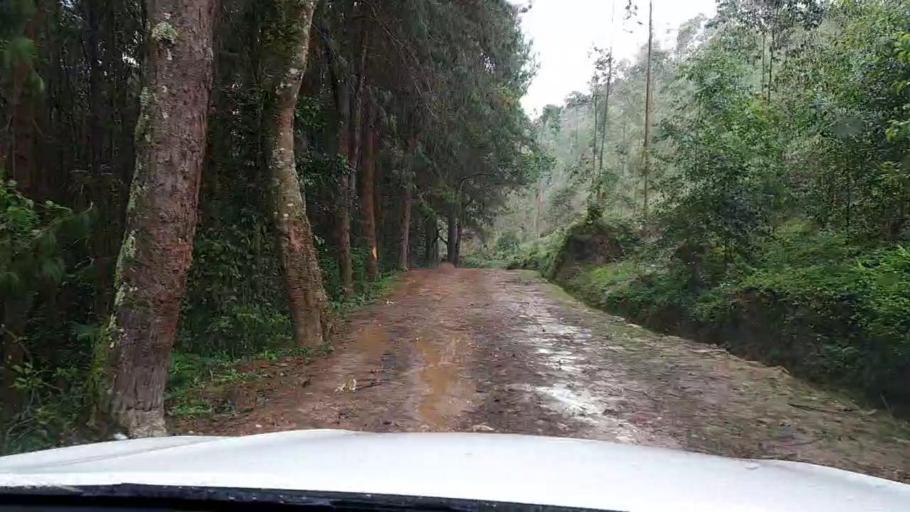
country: RW
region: Western Province
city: Cyangugu
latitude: -2.5528
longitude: 28.9774
